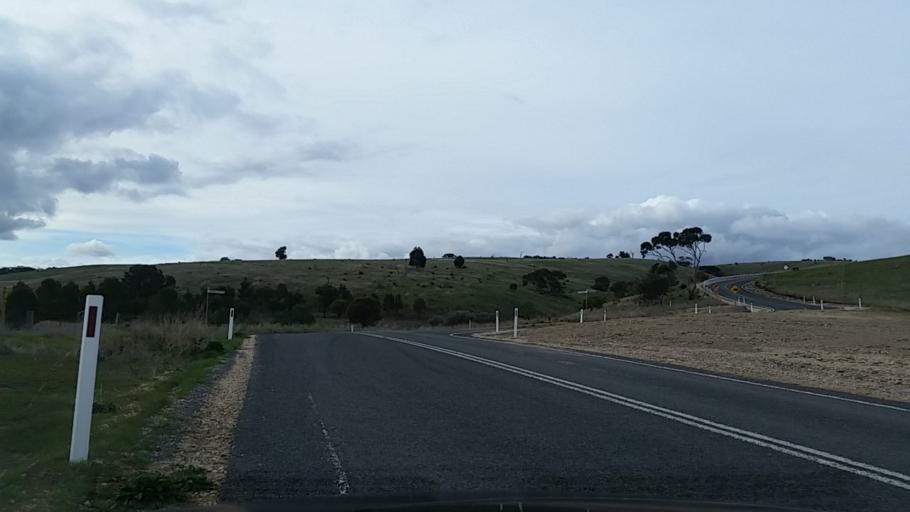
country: AU
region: South Australia
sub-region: Mount Barker
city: Callington
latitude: -35.0156
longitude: 139.0525
